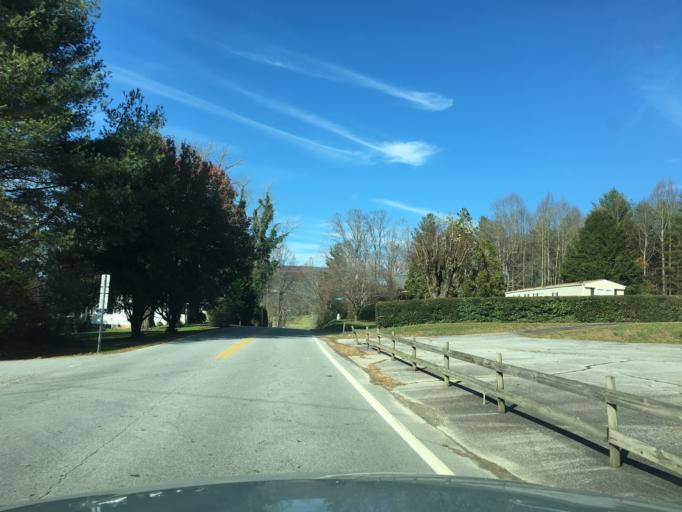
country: US
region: North Carolina
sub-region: Henderson County
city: Etowah
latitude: 35.2544
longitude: -82.6338
